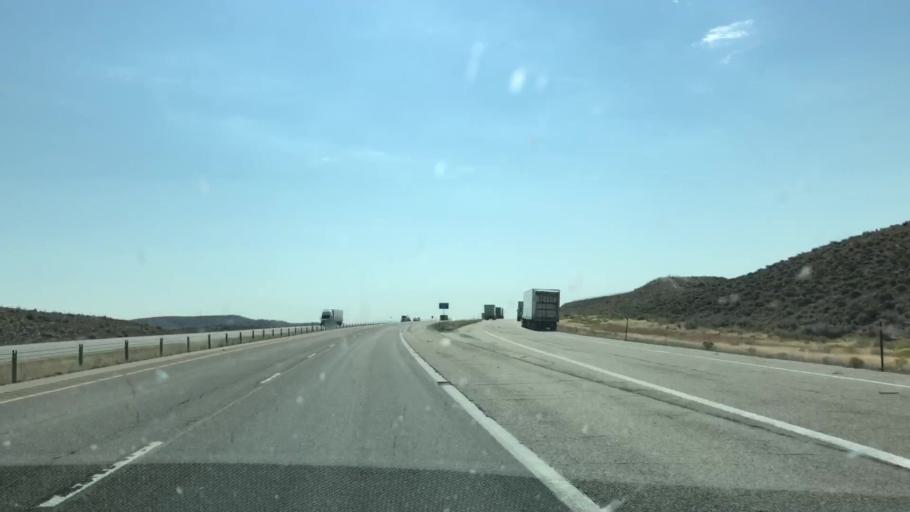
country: US
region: Wyoming
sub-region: Sweetwater County
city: Rock Springs
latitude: 41.6727
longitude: -108.7394
